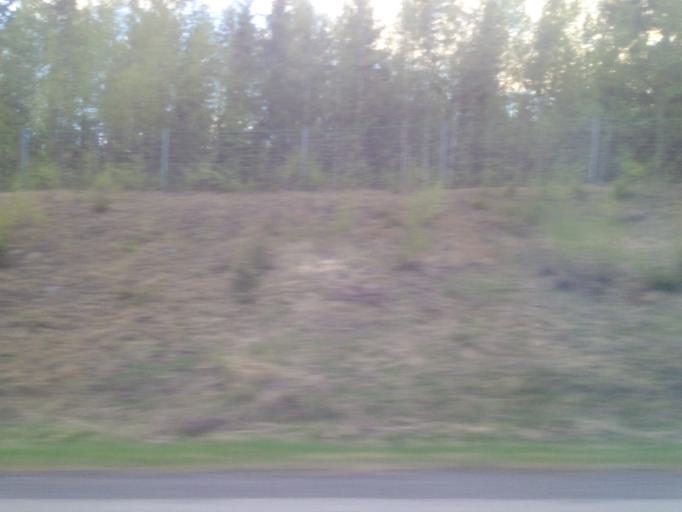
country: FI
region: Pirkanmaa
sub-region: Etelae-Pirkanmaa
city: Toijala
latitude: 61.2305
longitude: 23.8372
